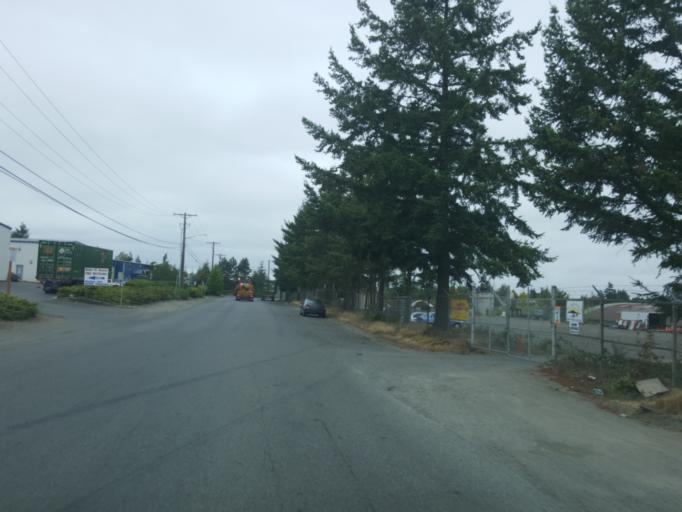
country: US
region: Washington
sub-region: Pierce County
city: McChord Air Force Base
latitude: 47.1627
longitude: -122.4709
